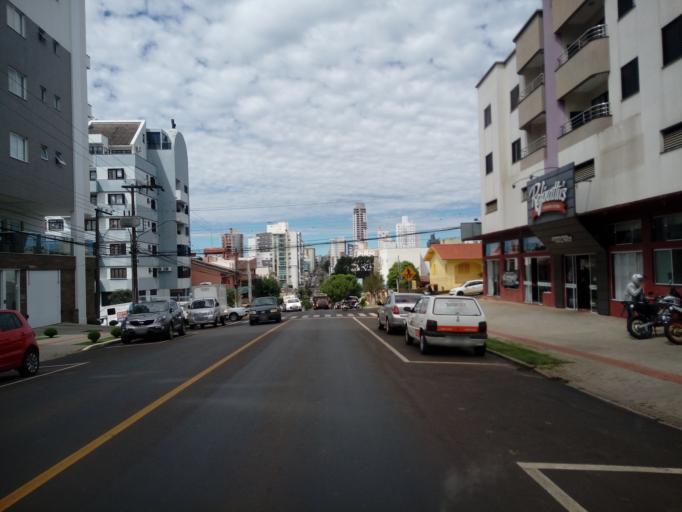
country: BR
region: Santa Catarina
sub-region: Chapeco
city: Chapeco
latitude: -27.0948
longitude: -52.6105
